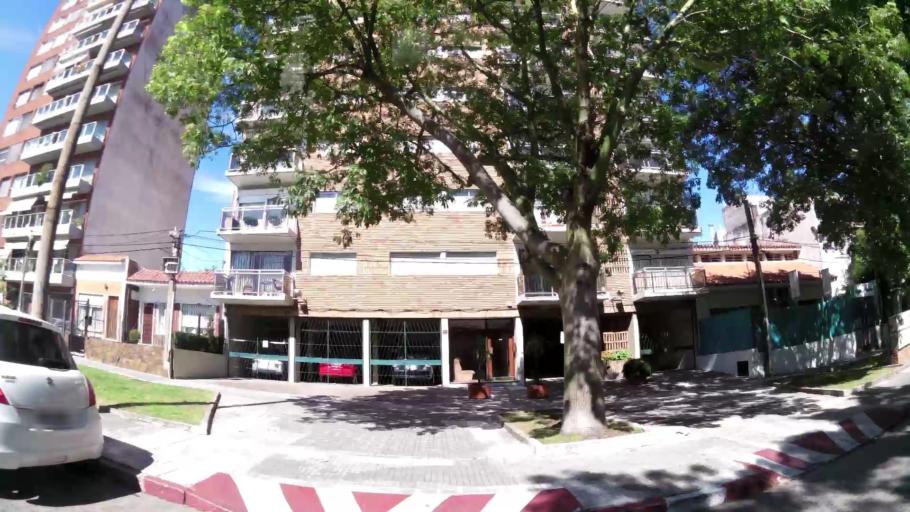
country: UY
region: Montevideo
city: Montevideo
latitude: -34.9017
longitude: -56.1567
